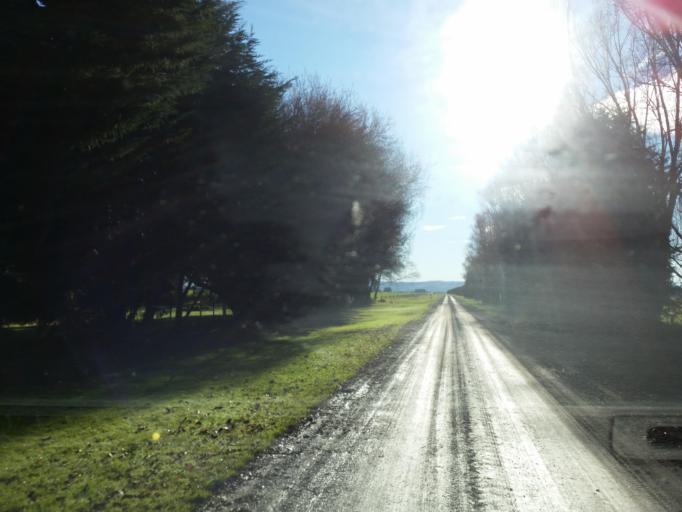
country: NZ
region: Southland
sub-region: Southland District
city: Winton
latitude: -46.1152
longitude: 168.1100
